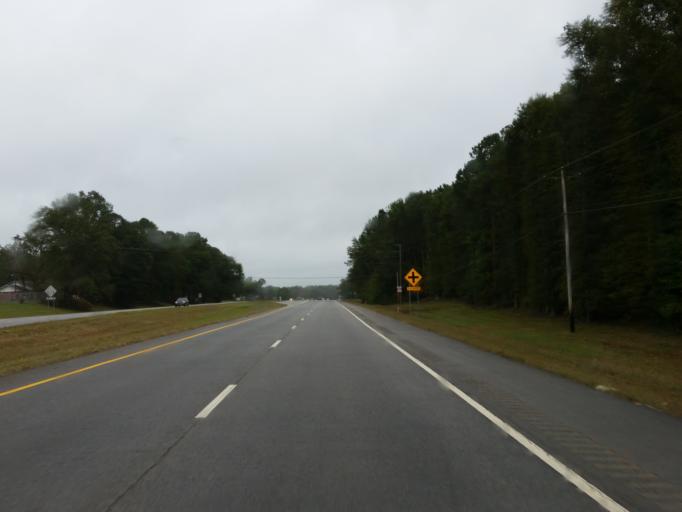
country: US
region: Georgia
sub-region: Lamar County
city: Barnesville
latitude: 33.1045
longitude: -84.1904
